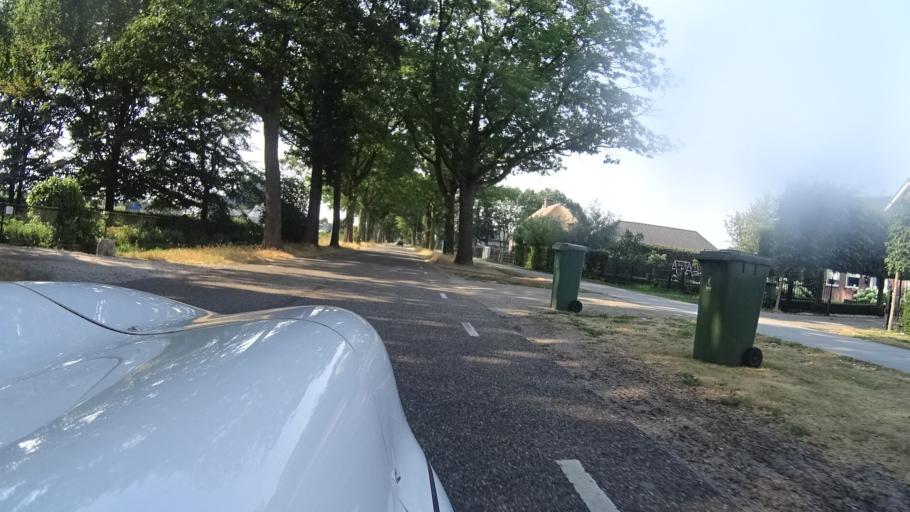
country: NL
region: North Brabant
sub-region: Gemeente Mill en Sint Hubert
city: Wilbertoord
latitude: 51.6477
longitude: 5.7779
